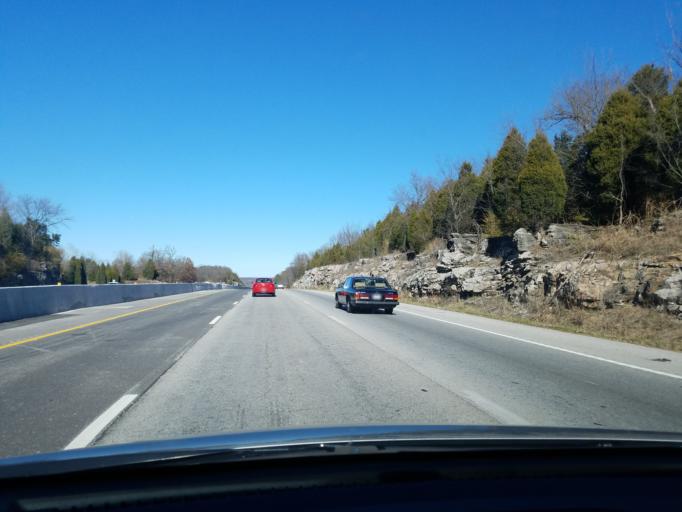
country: US
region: Missouri
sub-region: Christian County
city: Nixa
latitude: 37.1071
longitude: -93.2330
